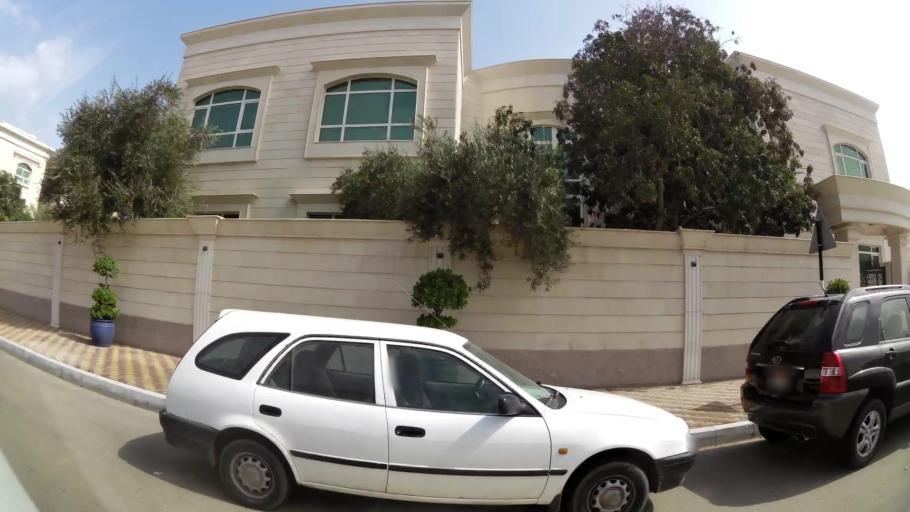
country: AE
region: Abu Dhabi
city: Abu Dhabi
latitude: 24.4440
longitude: 54.3595
